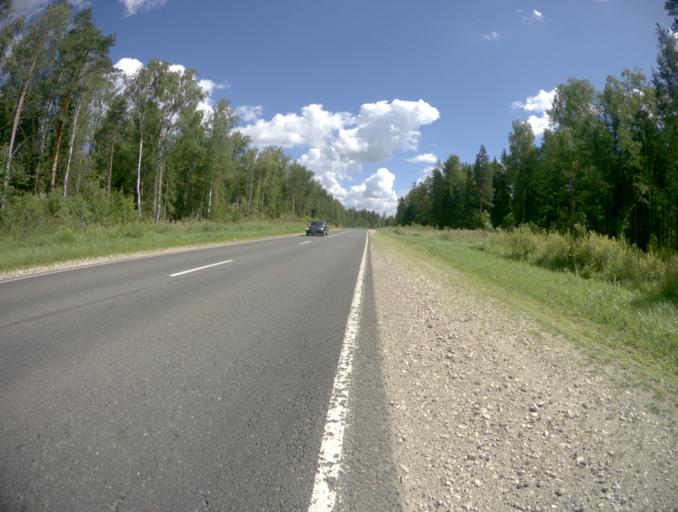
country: RU
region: Vladimir
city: Orgtrud
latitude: 56.0110
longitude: 40.6179
